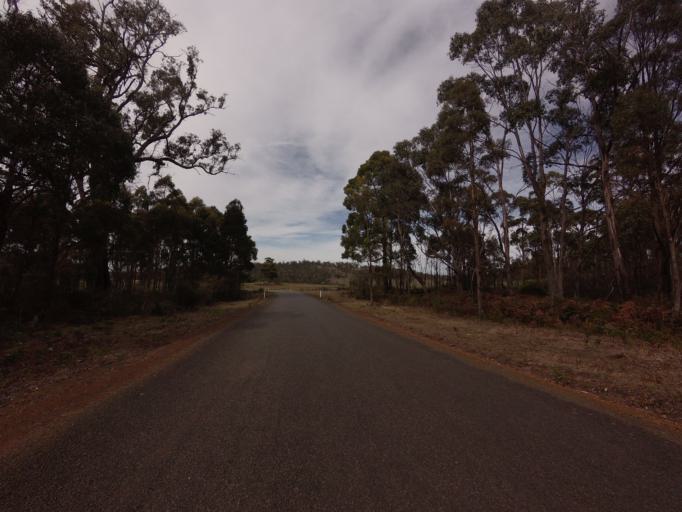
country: AU
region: Tasmania
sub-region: Sorell
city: Sorell
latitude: -42.5249
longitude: 147.6509
